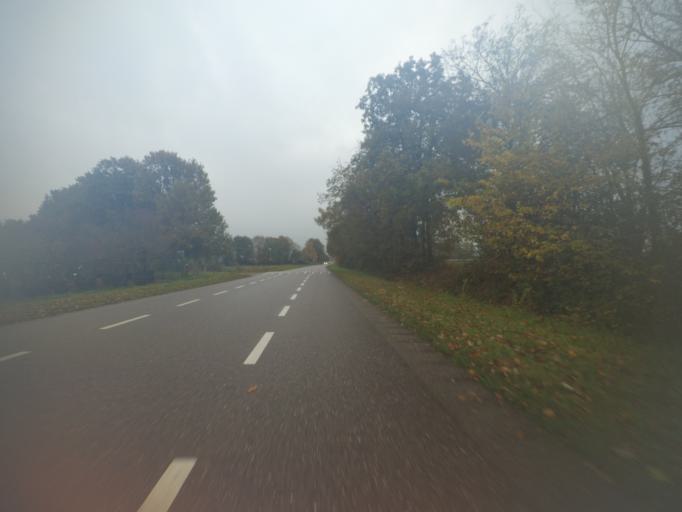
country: NL
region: Gelderland
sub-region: Gemeente Ede
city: Lunteren
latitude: 52.0974
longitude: 5.5928
